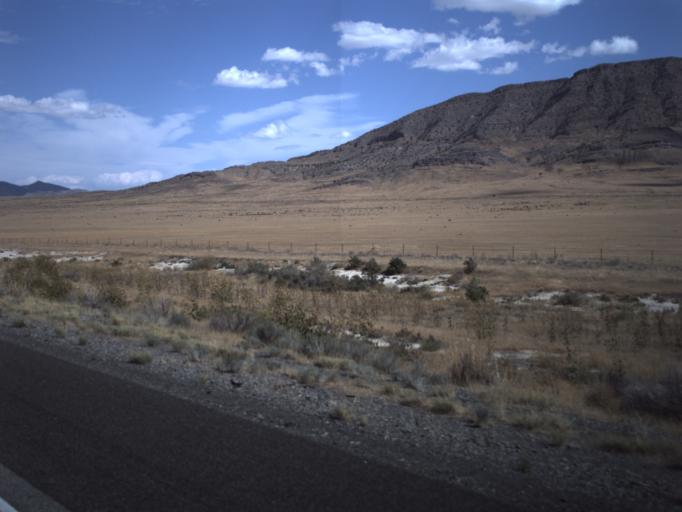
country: US
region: Utah
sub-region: Tooele County
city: Grantsville
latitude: 40.7852
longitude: -112.9619
